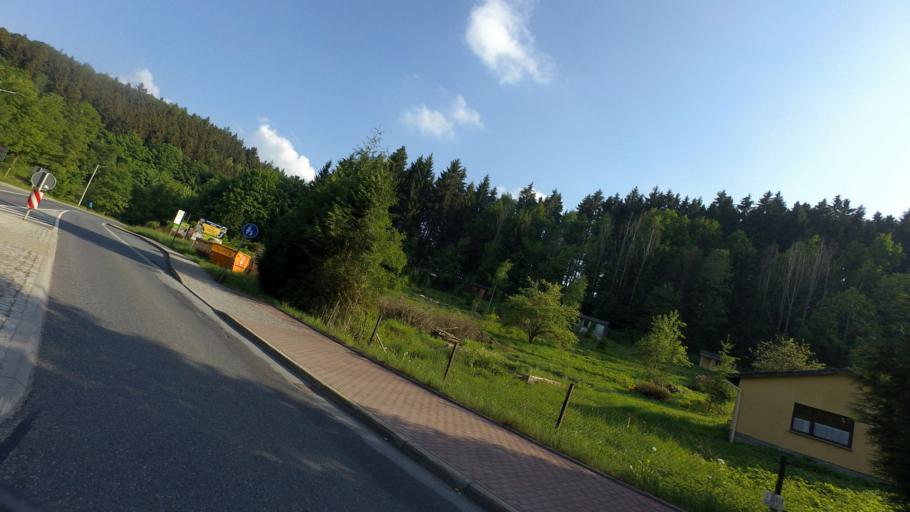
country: DE
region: Saxony
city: Sebnitz
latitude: 50.9832
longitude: 14.2617
